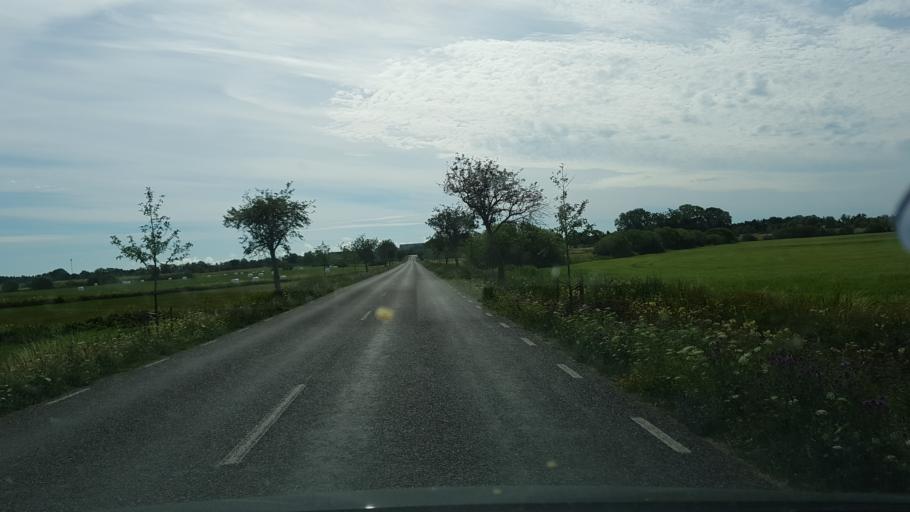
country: SE
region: Gotland
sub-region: Gotland
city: Hemse
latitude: 57.4318
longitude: 18.6202
